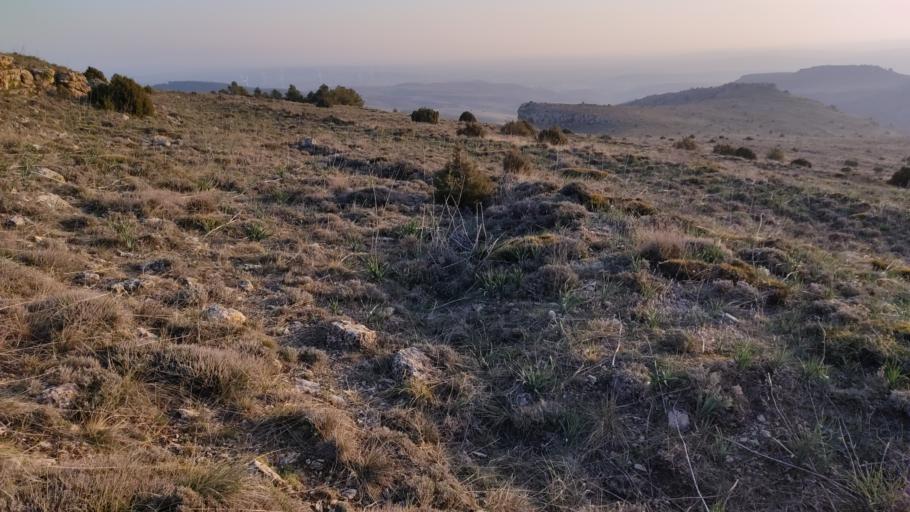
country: ES
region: Aragon
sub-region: Provincia de Teruel
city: Allueva
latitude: 41.0184
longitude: -1.0435
